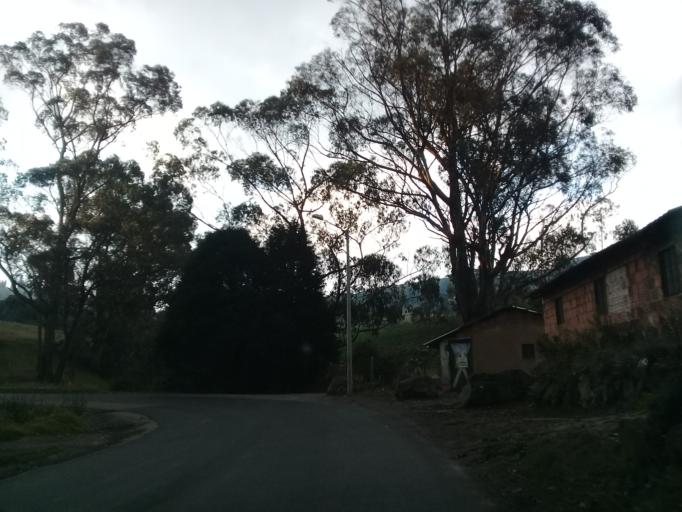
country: CO
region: Cundinamarca
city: Zipaquira
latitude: 5.0801
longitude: -74.0554
